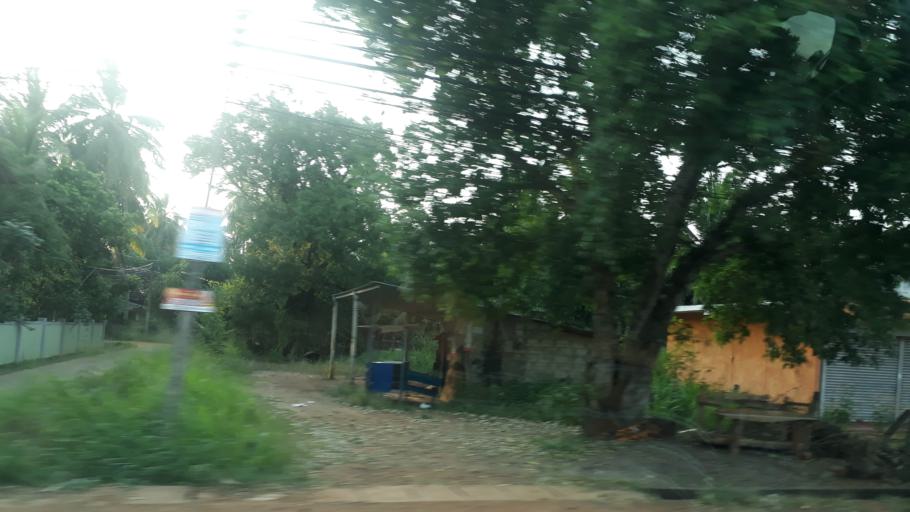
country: LK
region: North Central
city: Anuradhapura
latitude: 8.2988
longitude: 80.3764
